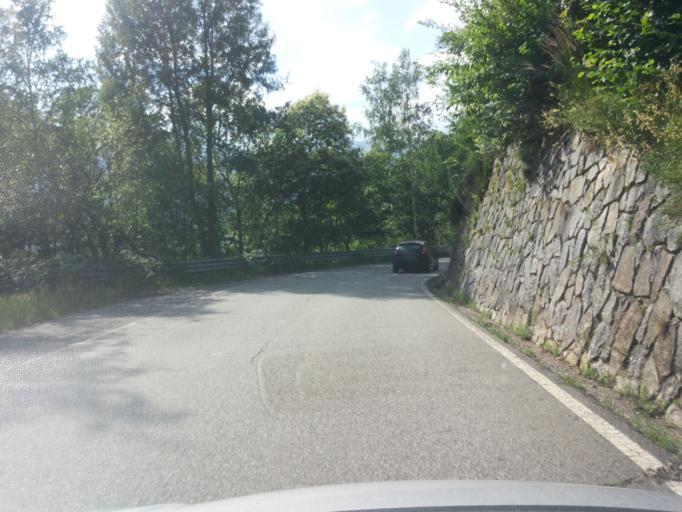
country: IT
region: Piedmont
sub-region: Provincia di Biella
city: Quittengo
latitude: 45.6639
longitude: 8.0121
